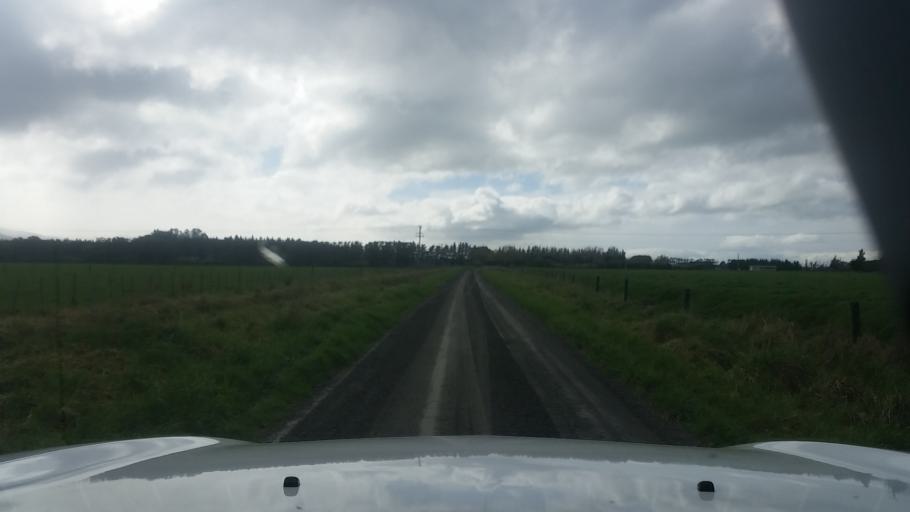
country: NZ
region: Wellington
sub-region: South Wairarapa District
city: Waipawa
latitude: -41.1456
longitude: 175.4033
